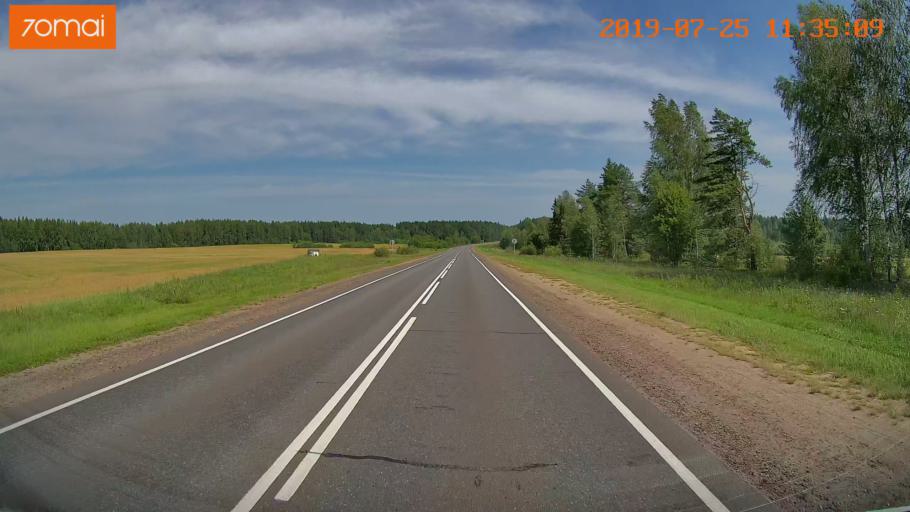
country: RU
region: Ivanovo
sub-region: Privolzhskiy Rayon
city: Ples
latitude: 57.4086
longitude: 41.4245
